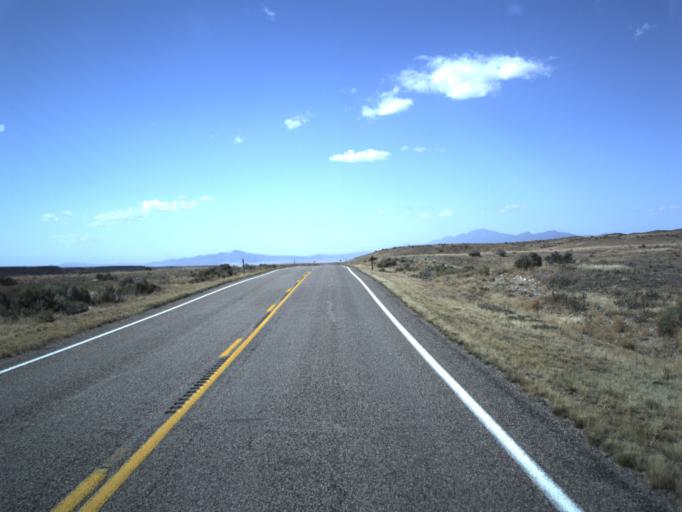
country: US
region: Utah
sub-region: Beaver County
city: Milford
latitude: 38.7792
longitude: -112.9256
